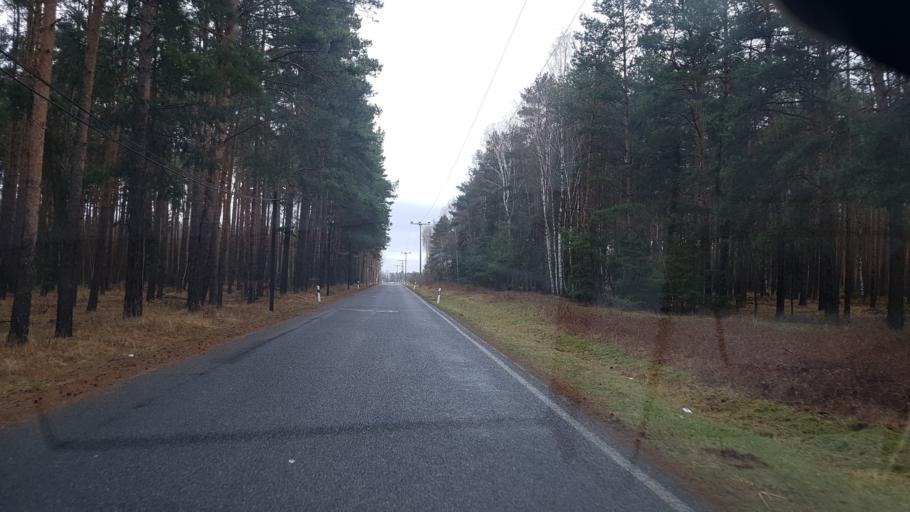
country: DE
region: Brandenburg
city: Neupetershain
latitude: 51.6141
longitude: 14.1292
